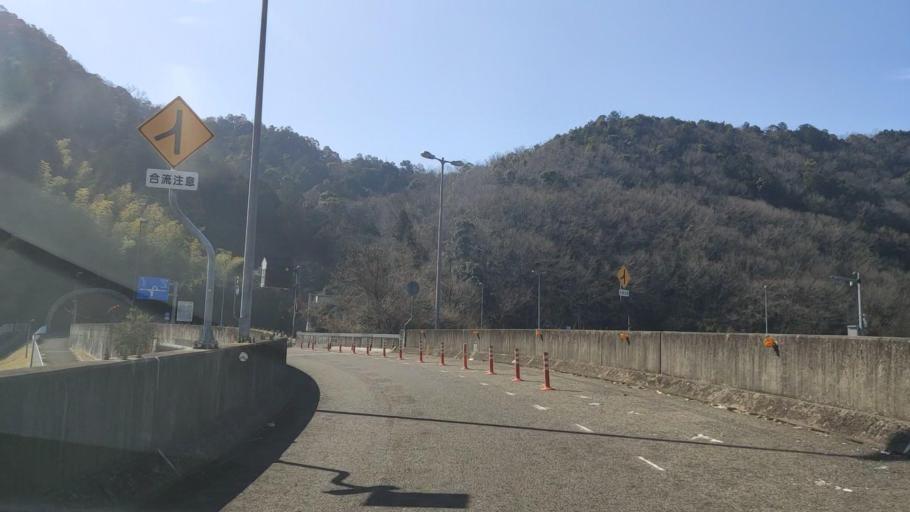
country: JP
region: Gifu
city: Gifu-shi
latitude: 35.4368
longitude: 136.7977
